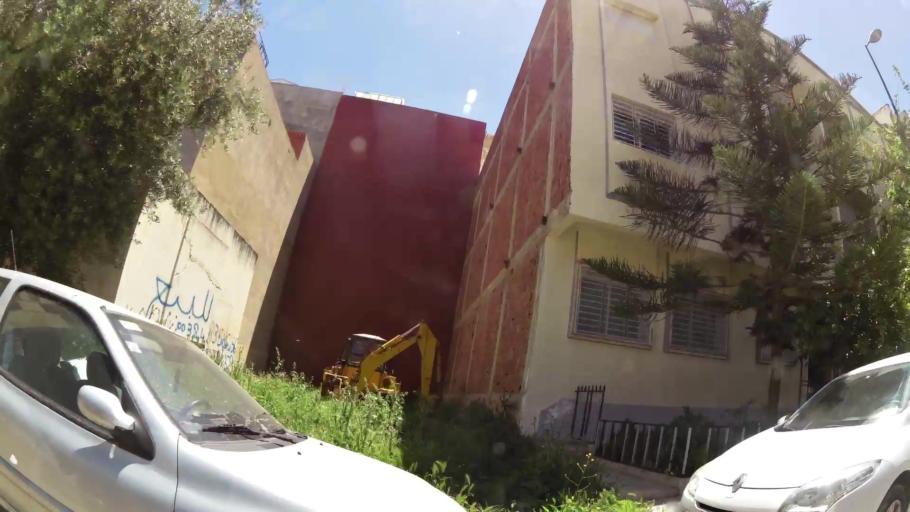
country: MA
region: Meknes-Tafilalet
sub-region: Meknes
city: Meknes
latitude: 33.8652
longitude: -5.5753
